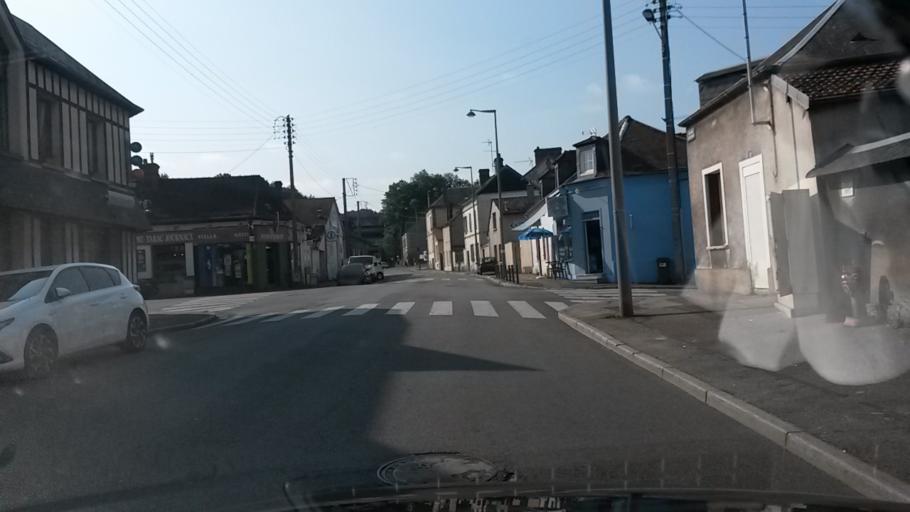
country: FR
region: Haute-Normandie
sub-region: Departement de l'Eure
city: Evreux
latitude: 49.0198
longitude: 1.1419
